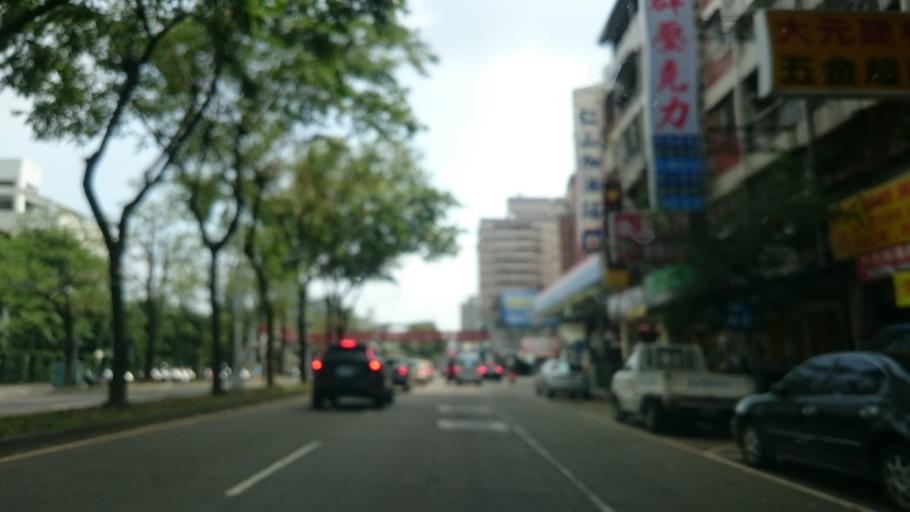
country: TW
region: Taiwan
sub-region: Taichung City
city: Taichung
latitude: 24.1348
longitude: 120.6572
